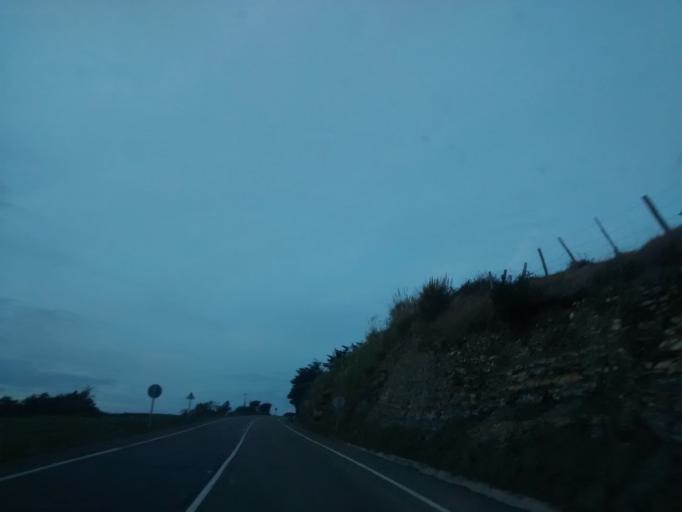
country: ES
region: Cantabria
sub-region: Provincia de Cantabria
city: Santa Cruz de Bezana
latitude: 43.4405
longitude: -3.9490
